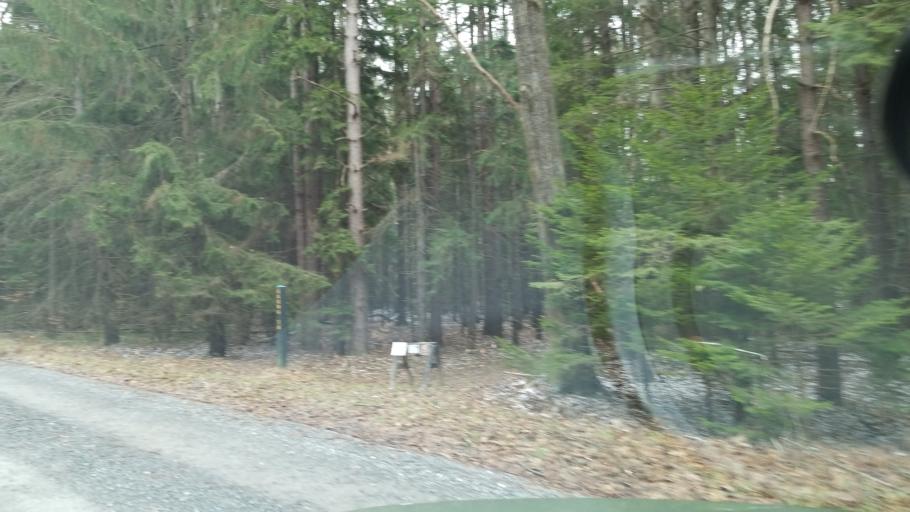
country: US
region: Pennsylvania
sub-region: Clearfield County
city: Clearfield
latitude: 41.1893
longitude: -78.5142
